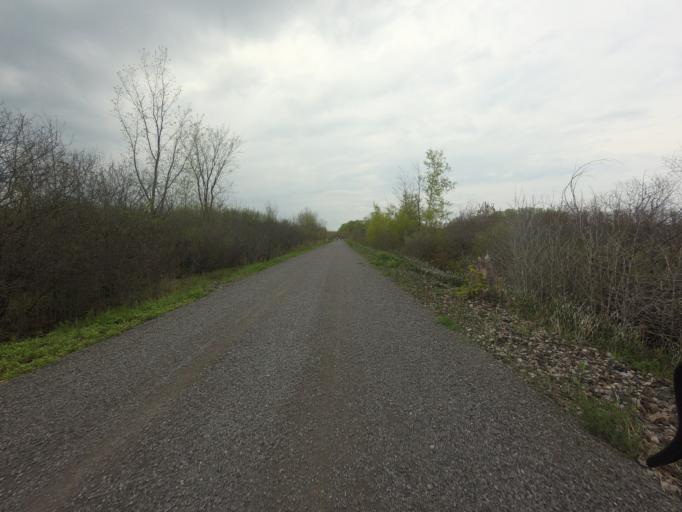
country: CA
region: Ontario
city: Carleton Place
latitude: 45.2183
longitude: -76.1849
